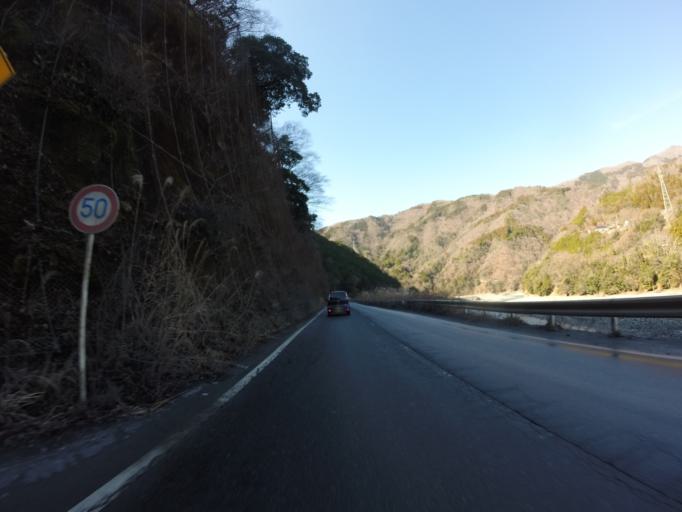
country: JP
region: Yamanashi
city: Ryuo
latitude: 35.4216
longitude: 138.3923
